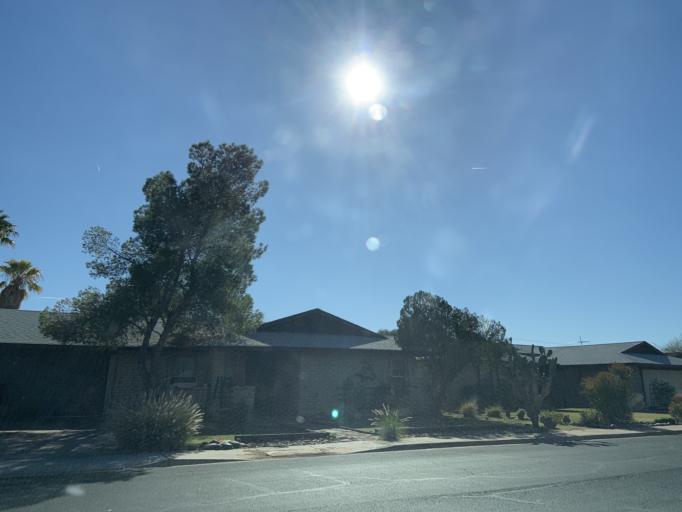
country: US
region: Arizona
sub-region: Maricopa County
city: San Carlos
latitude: 33.3600
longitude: -111.8663
